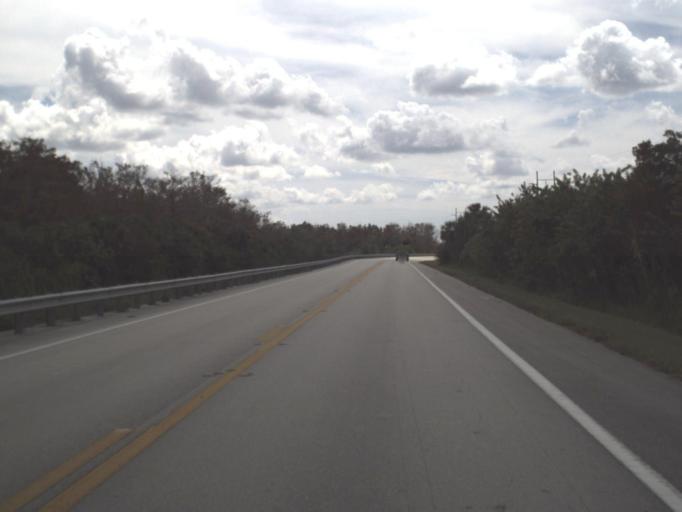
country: US
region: Florida
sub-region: Collier County
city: Marco
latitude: 25.9233
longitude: -81.3581
